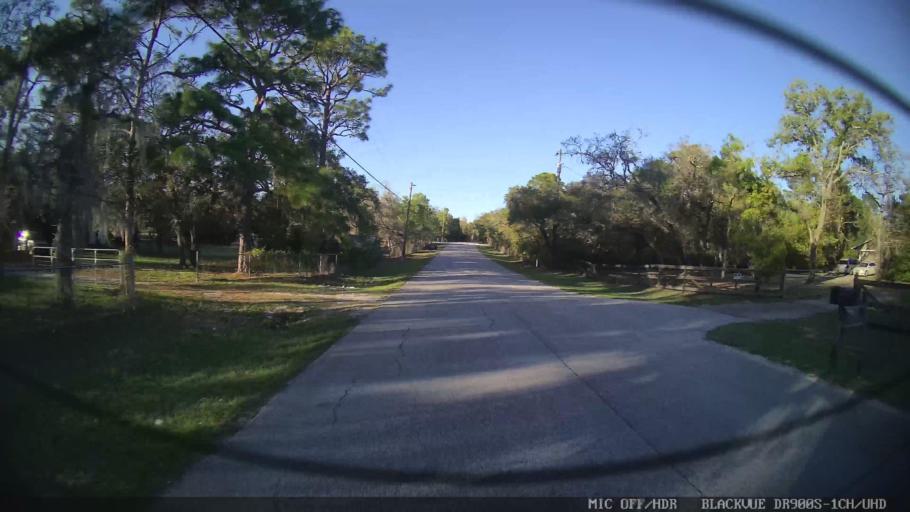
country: US
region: Florida
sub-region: Pasco County
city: Shady Hills
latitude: 28.4156
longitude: -82.5730
